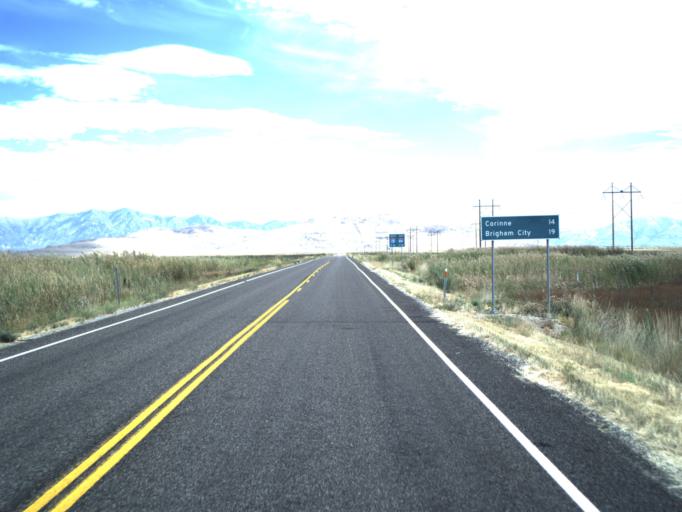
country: US
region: Utah
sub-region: Box Elder County
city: Tremonton
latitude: 41.6126
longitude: -112.3652
